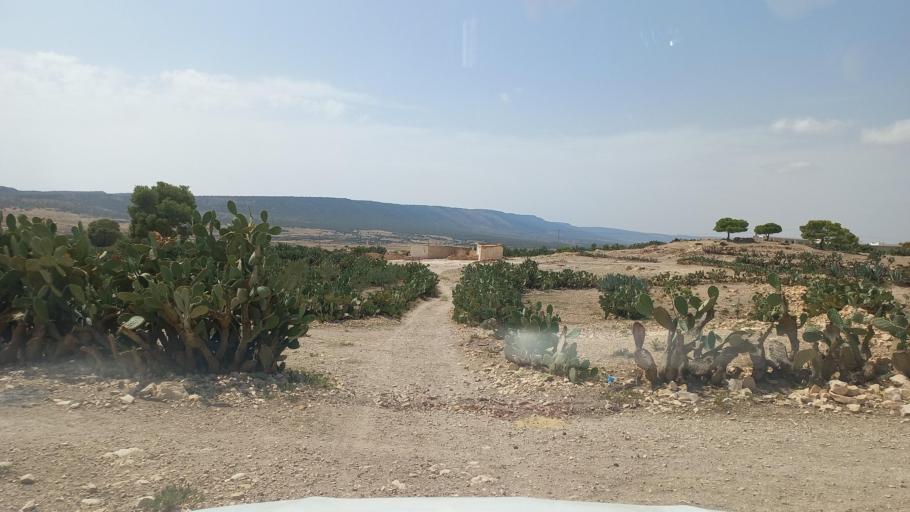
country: TN
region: Al Qasrayn
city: Sbiba
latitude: 35.4052
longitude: 8.9742
